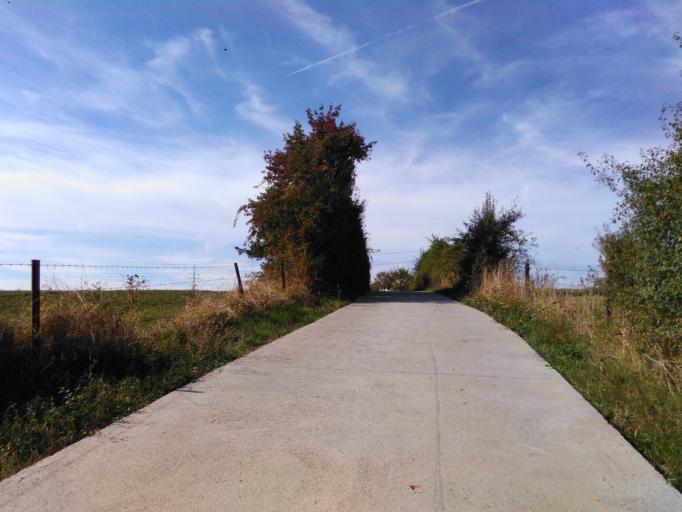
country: LU
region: Luxembourg
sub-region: Canton d'Esch-sur-Alzette
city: Sanem
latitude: 49.5508
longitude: 5.9166
